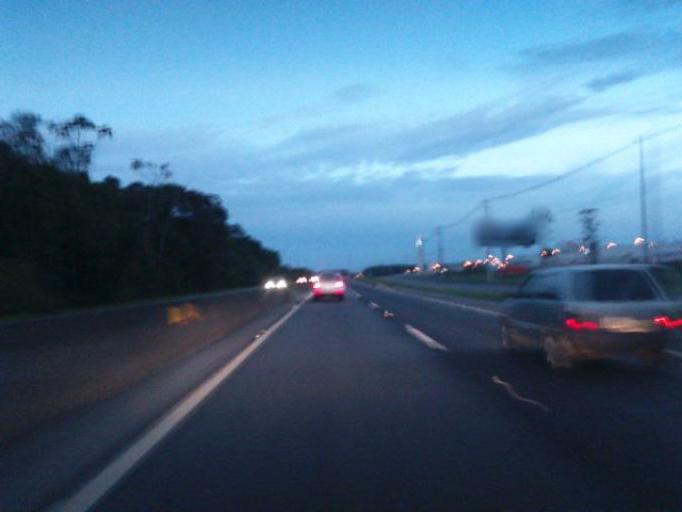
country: BR
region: Santa Catarina
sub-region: Barra Velha
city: Barra Velha
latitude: -26.4756
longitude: -48.7409
